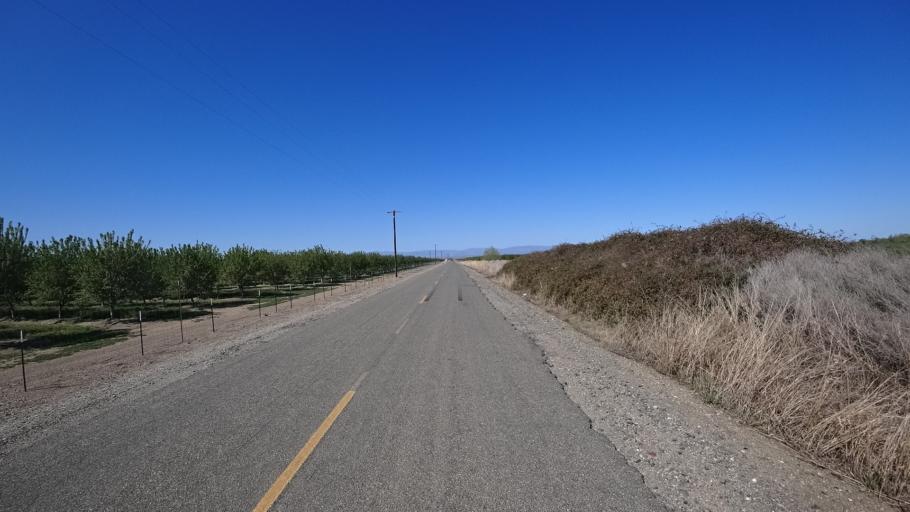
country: US
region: California
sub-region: Glenn County
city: Orland
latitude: 39.6972
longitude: -122.2302
